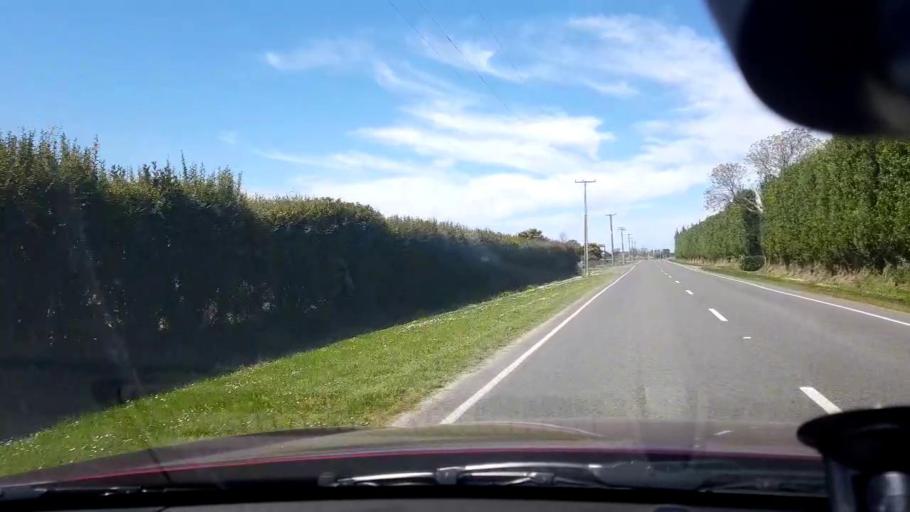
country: NZ
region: Gisborne
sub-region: Gisborne District
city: Gisborne
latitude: -38.6278
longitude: 177.9252
